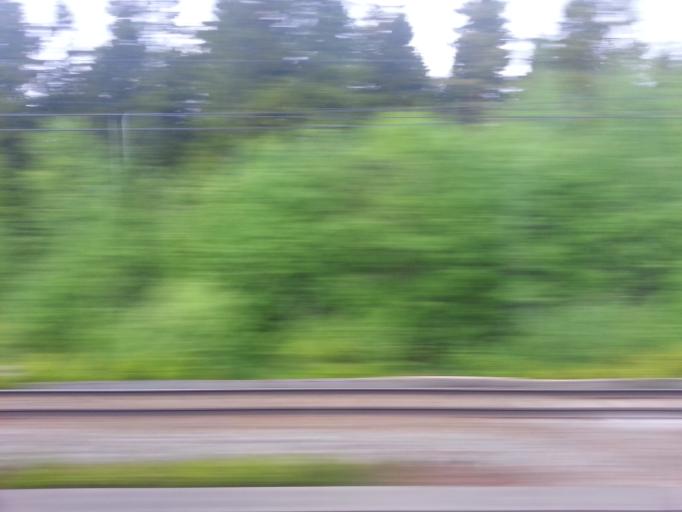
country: NO
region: Akershus
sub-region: Ullensaker
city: Klofta
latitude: 60.0537
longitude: 11.1376
